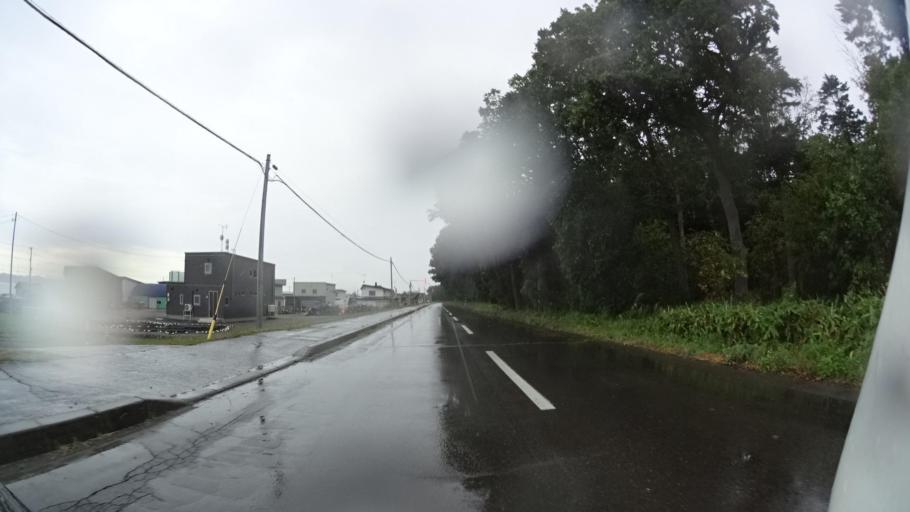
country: JP
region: Hokkaido
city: Mombetsu
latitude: 44.3285
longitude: 143.4956
